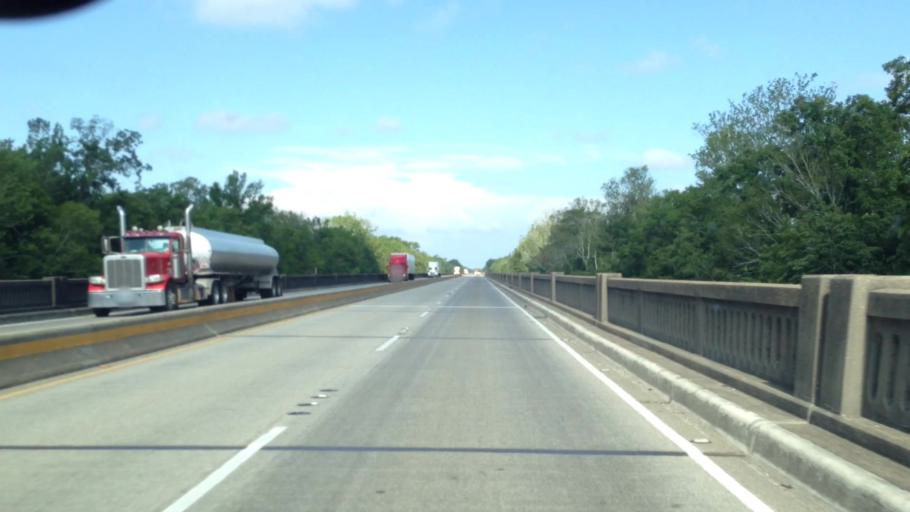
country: US
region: Louisiana
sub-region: Saint Landry Parish
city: Krotz Springs
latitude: 30.5550
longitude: -91.6839
